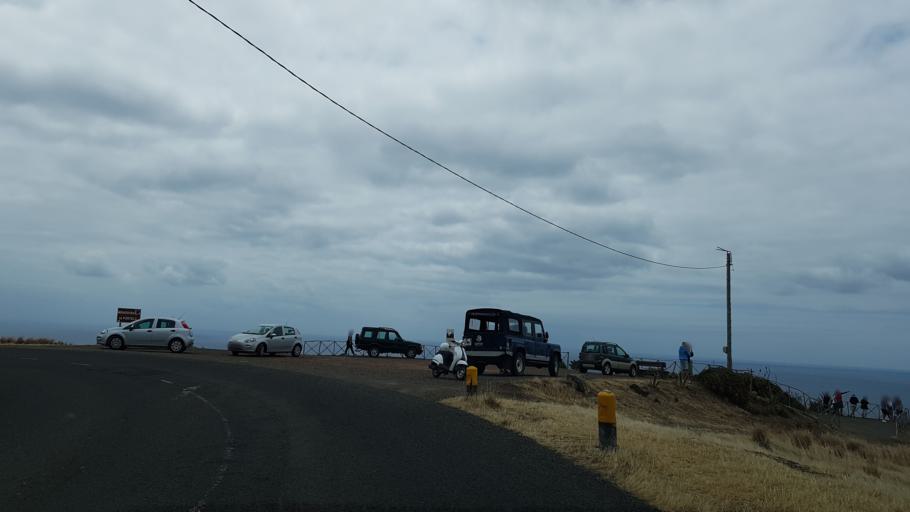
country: PT
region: Madeira
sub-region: Porto Santo
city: Vila de Porto Santo
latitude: 33.0668
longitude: -16.3176
